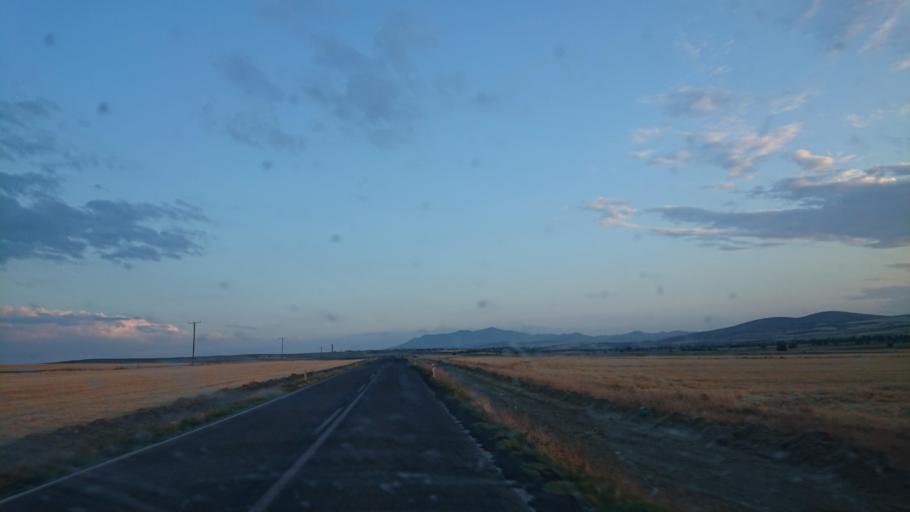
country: TR
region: Aksaray
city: Balci
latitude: 38.8207
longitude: 34.1355
